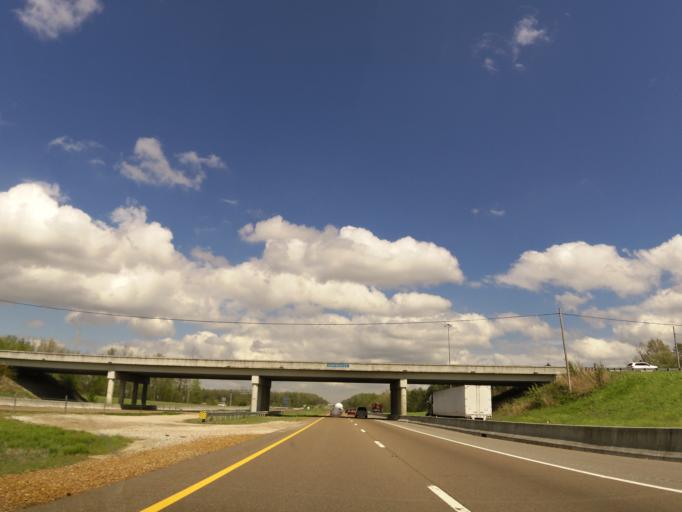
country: US
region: Tennessee
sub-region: Shelby County
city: Arlington
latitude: 35.2617
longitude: -89.6658
